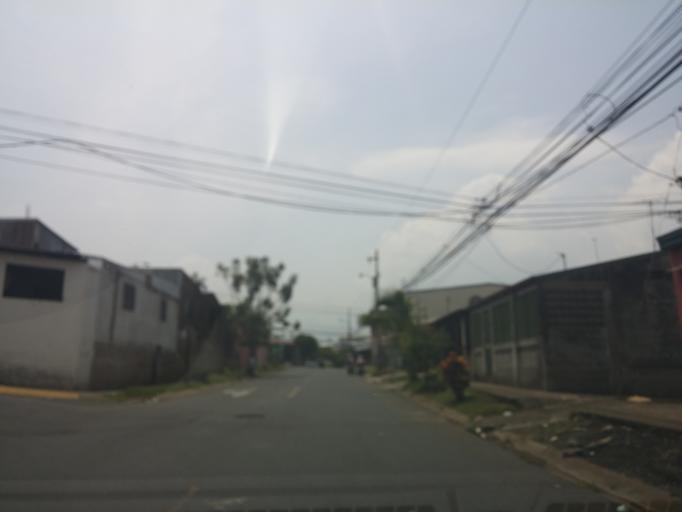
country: CR
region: Heredia
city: San Francisco
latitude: 9.9800
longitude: -84.1170
